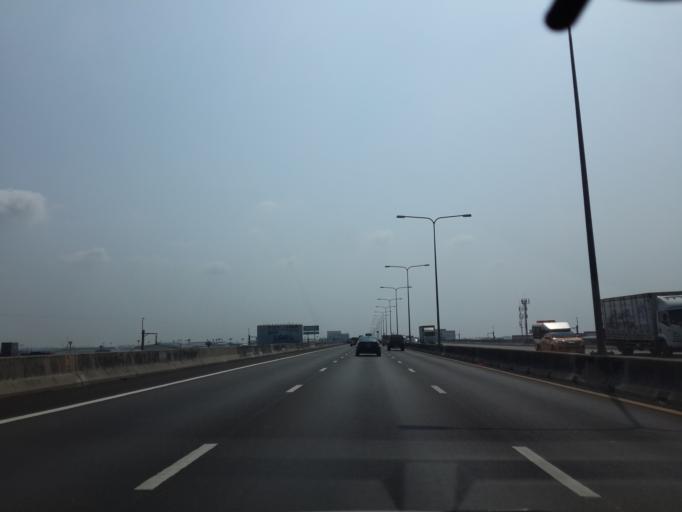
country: TH
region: Samut Prakan
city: Bang Bo District
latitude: 13.6014
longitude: 100.7867
